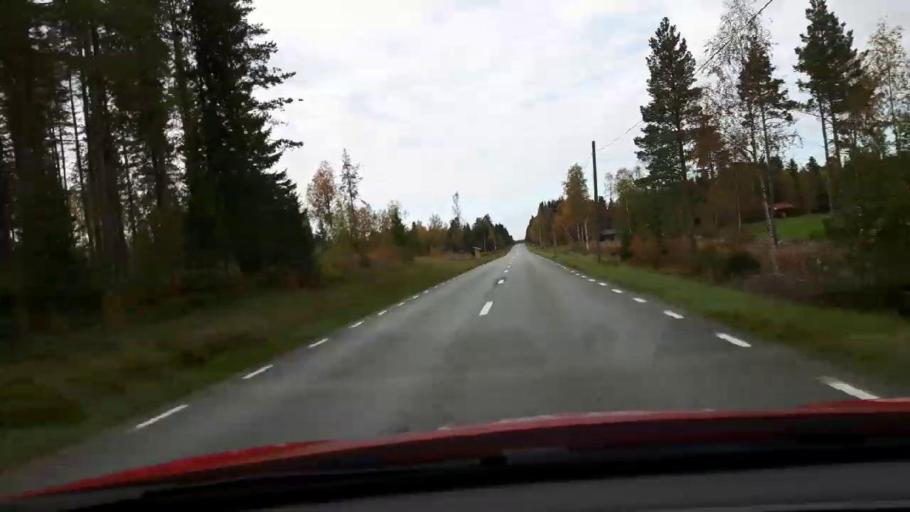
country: SE
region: Jaemtland
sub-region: Krokoms Kommun
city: Krokom
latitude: 63.1935
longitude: 14.0533
